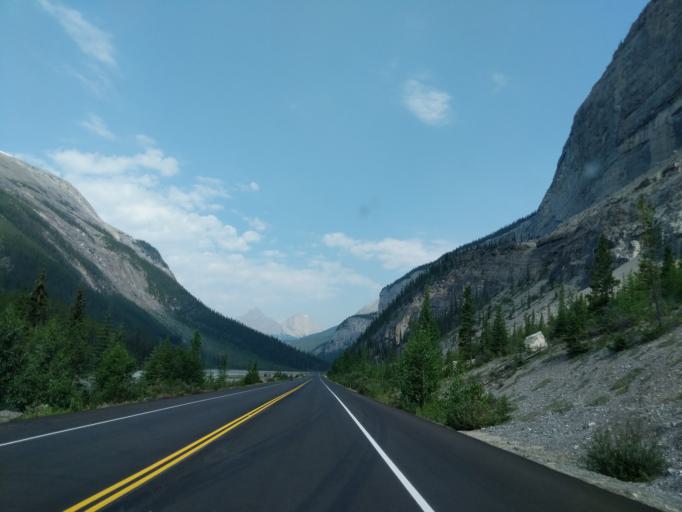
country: CA
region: British Columbia
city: Golden
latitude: 52.1427
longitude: -116.9955
